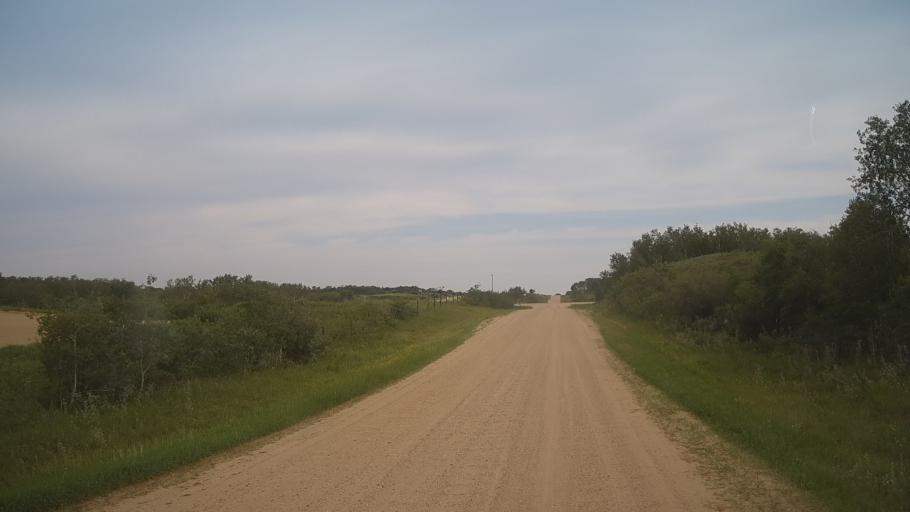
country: CA
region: Saskatchewan
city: Saskatoon
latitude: 51.8517
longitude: -106.5208
